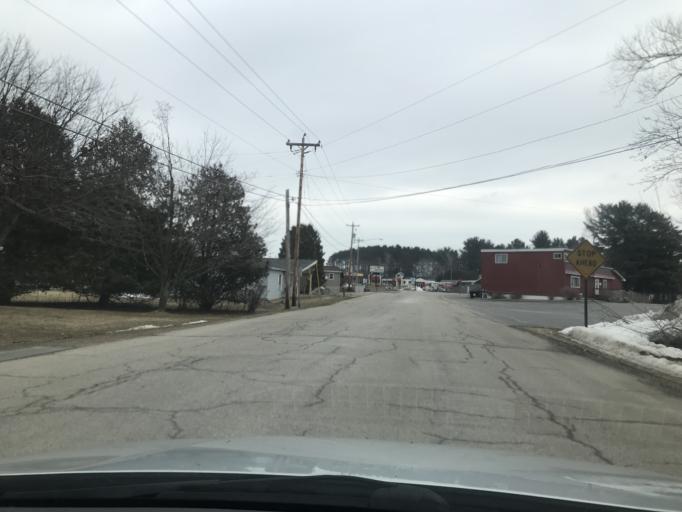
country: US
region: Wisconsin
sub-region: Marinette County
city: Peshtigo
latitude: 45.0550
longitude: -87.7646
